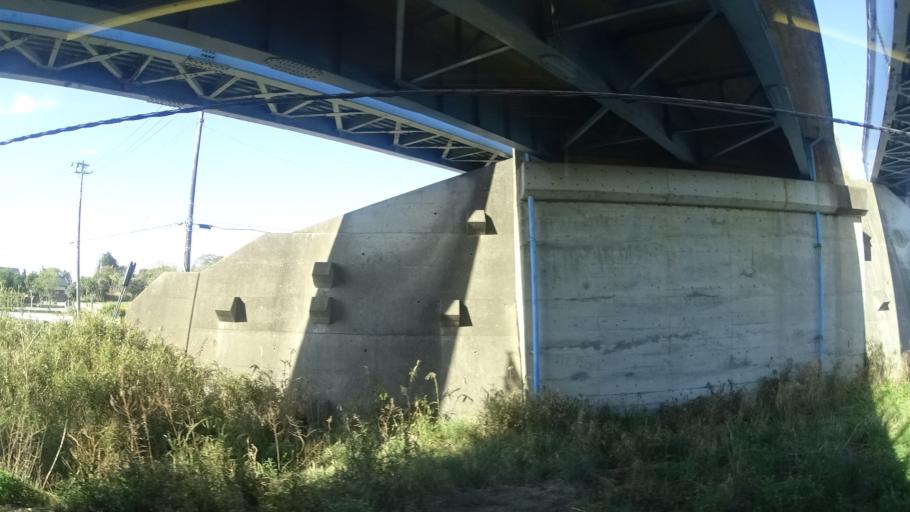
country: JP
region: Fukushima
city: Namie
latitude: 37.4958
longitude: 140.9836
